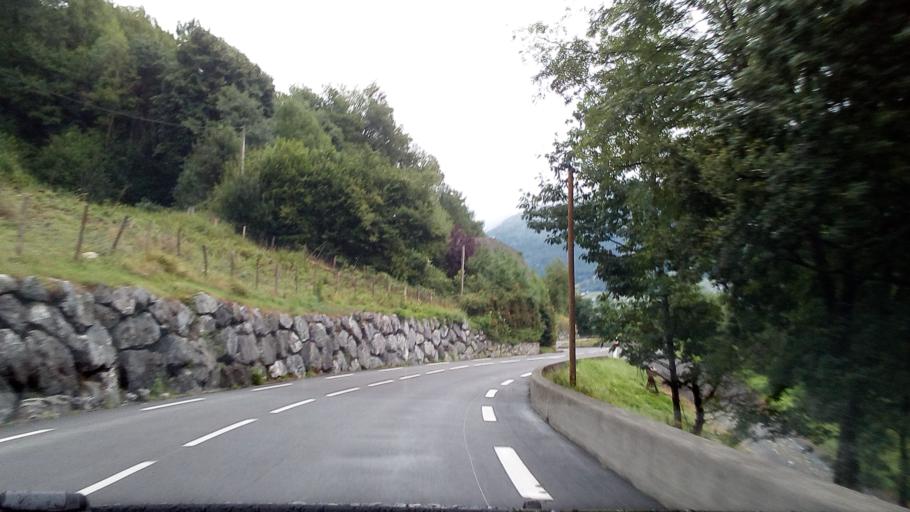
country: FR
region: Midi-Pyrenees
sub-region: Departement des Hautes-Pyrenees
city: Argeles-Gazost
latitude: 42.9985
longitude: -0.1159
